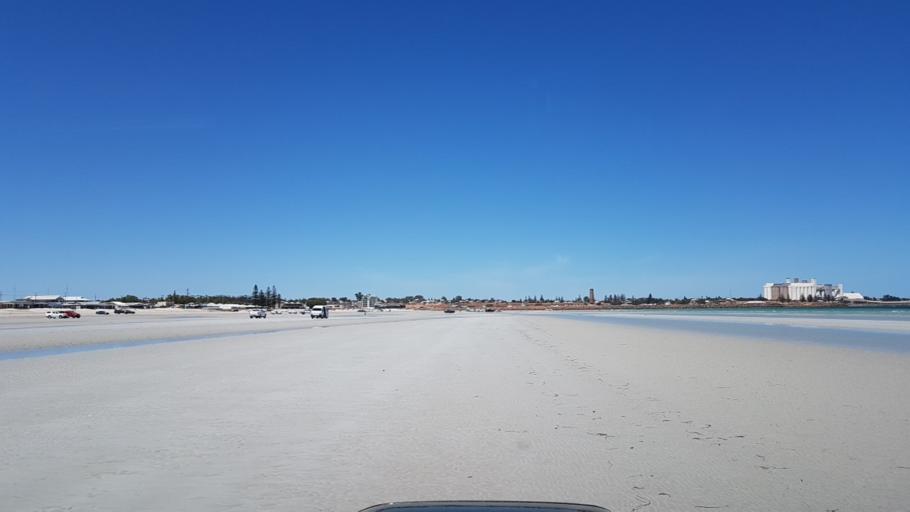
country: AU
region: South Australia
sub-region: Copper Coast
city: Wallaroo
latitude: -33.9135
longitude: 137.6295
